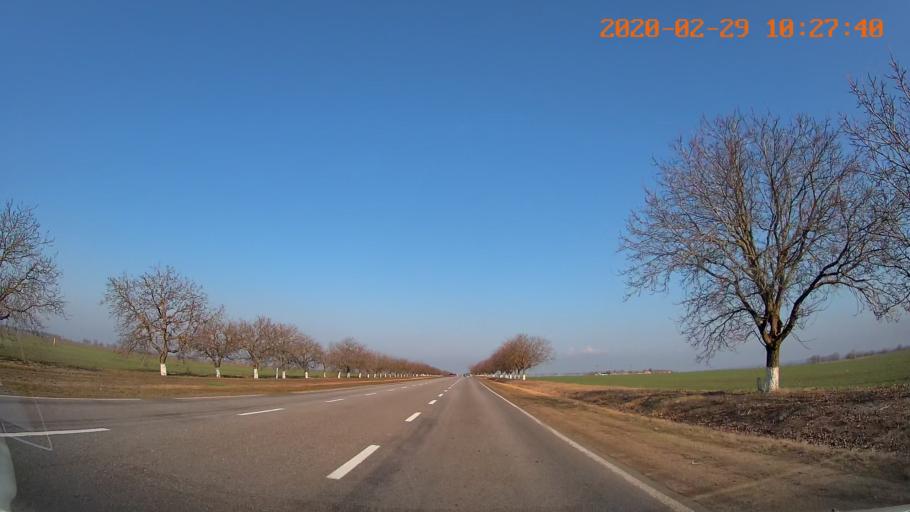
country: MD
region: Telenesti
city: Tiraspolul Nou
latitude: 46.8993
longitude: 29.5963
